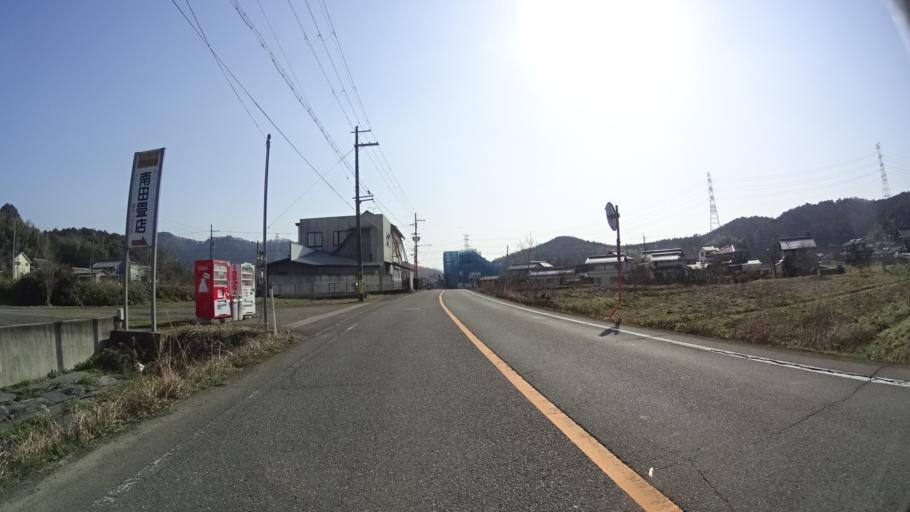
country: JP
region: Kyoto
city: Ayabe
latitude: 35.3546
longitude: 135.2213
